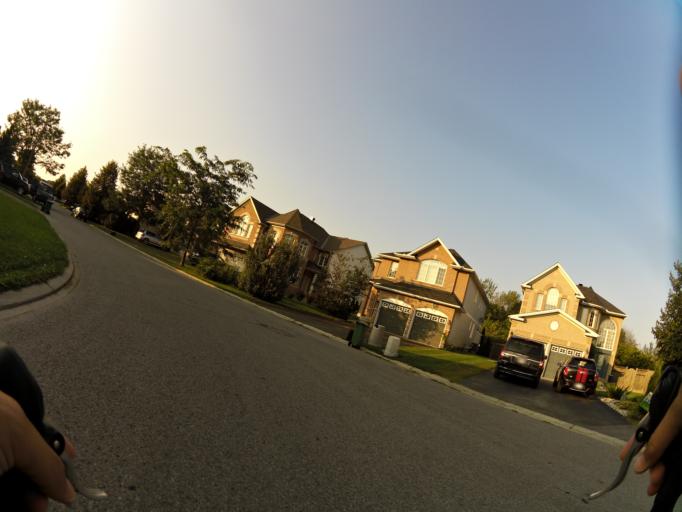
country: CA
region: Ontario
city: Bells Corners
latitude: 45.3554
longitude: -75.9184
